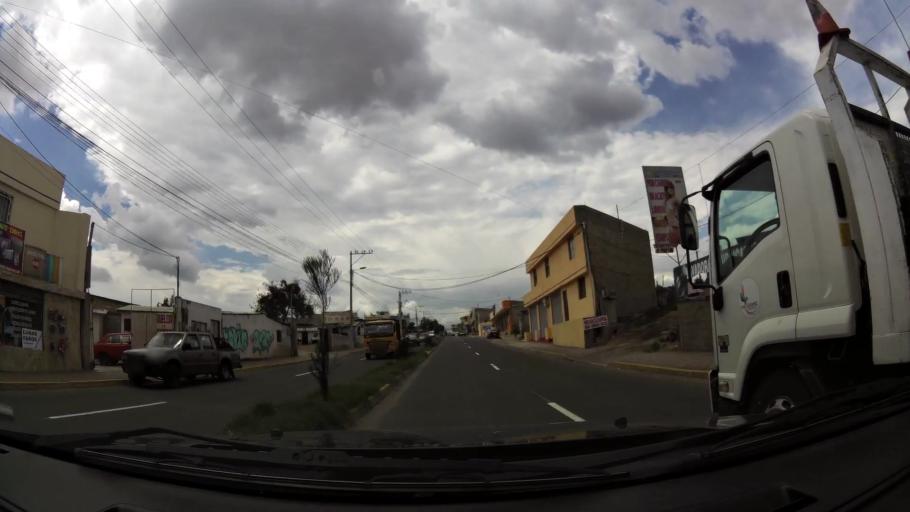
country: EC
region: Pichincha
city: Quito
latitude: -0.0985
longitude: -78.4439
